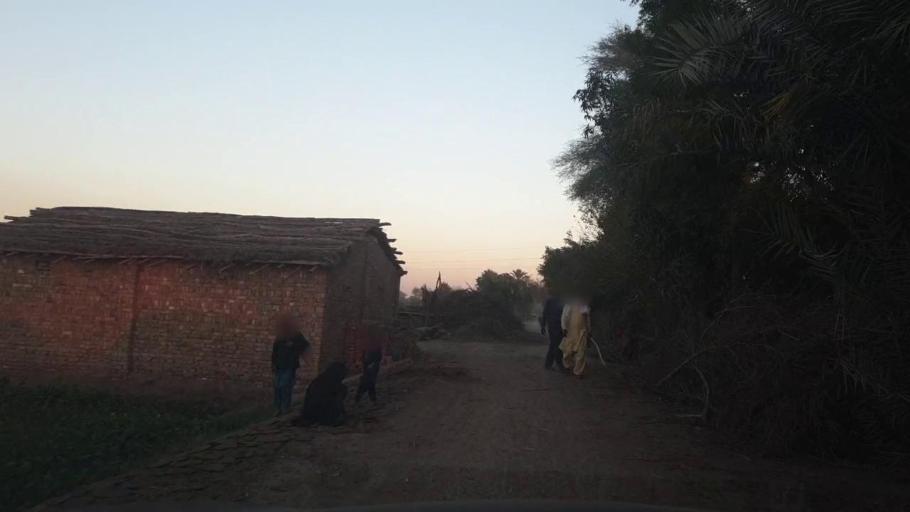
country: PK
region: Sindh
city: Ghotki
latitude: 28.0108
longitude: 69.3763
